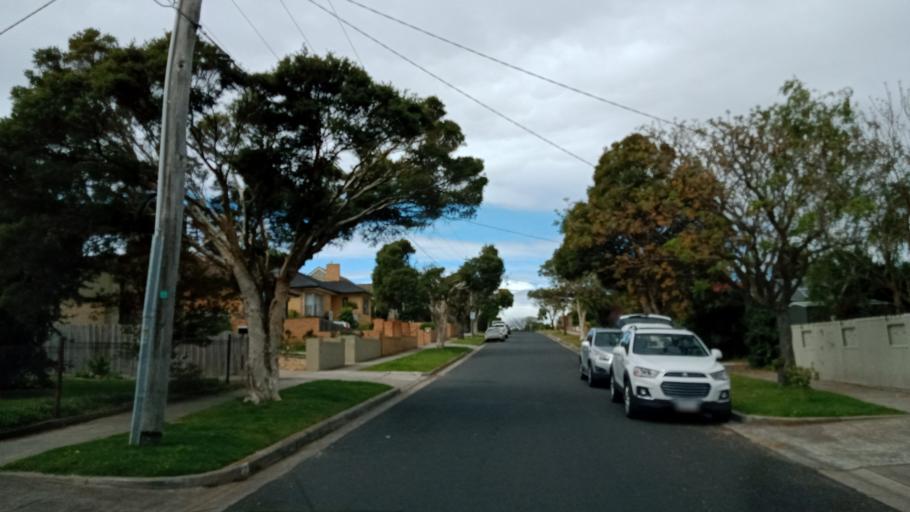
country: AU
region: Victoria
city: Highett
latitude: -37.9351
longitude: 145.0580
